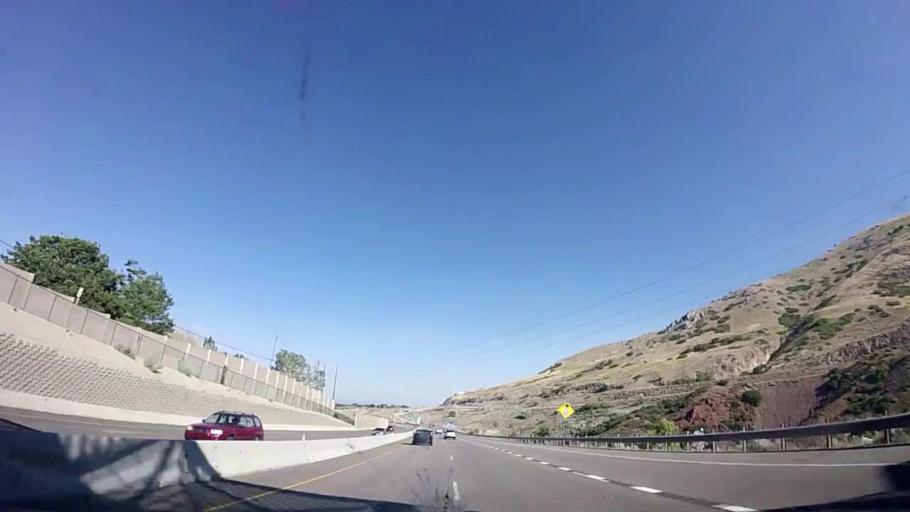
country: US
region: Utah
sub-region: Salt Lake County
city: East Millcreek
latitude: 40.7079
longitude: -111.7976
